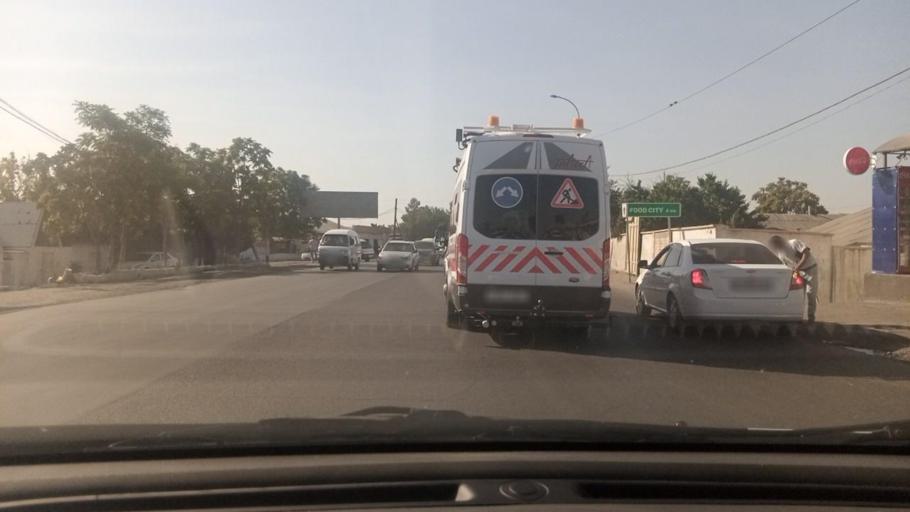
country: UZ
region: Toshkent Shahri
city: Bektemir
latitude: 41.2324
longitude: 69.3351
